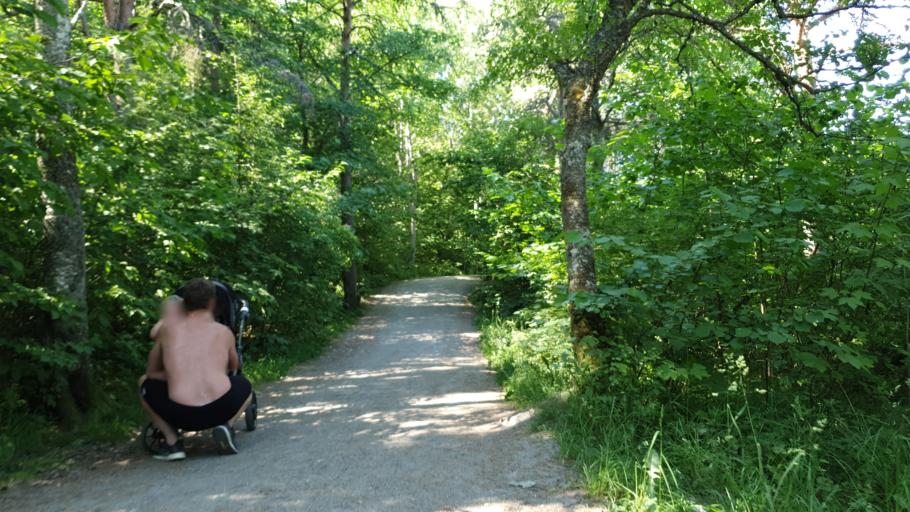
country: NO
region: Sor-Trondelag
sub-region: Trondheim
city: Trondheim
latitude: 63.4474
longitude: 10.4671
